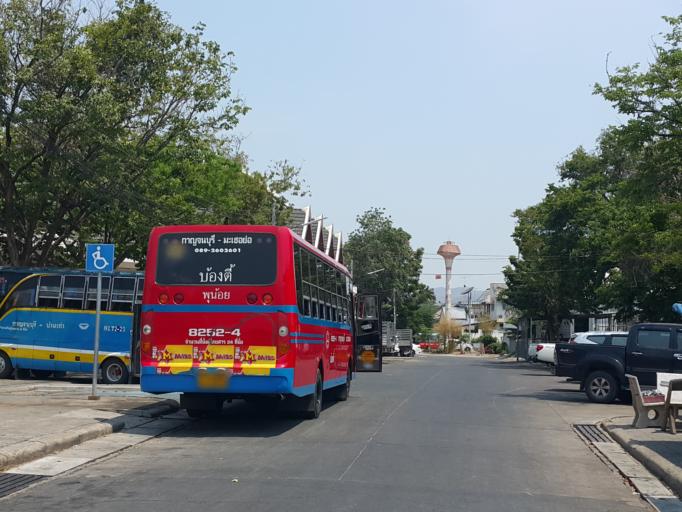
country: TH
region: Kanchanaburi
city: Kanchanaburi
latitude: 14.0222
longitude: 99.5280
